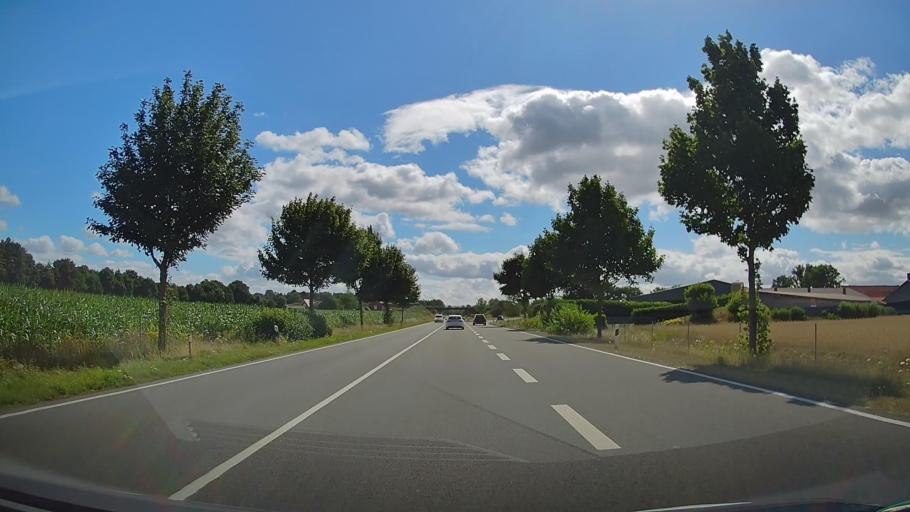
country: DE
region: Lower Saxony
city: Vechta
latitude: 52.7044
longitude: 8.2754
